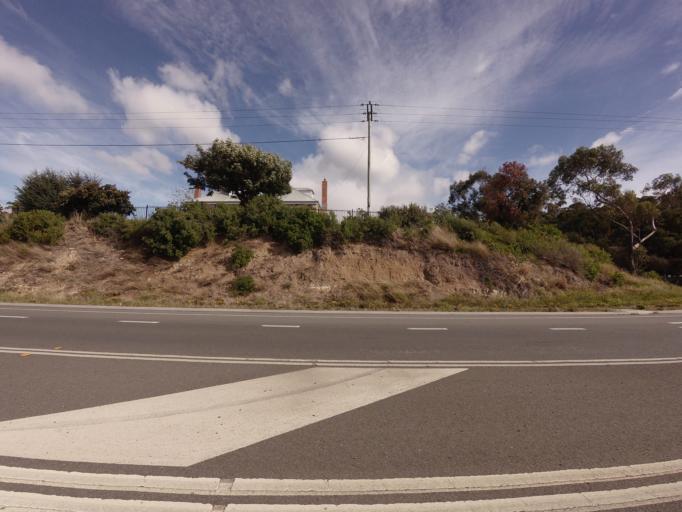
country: AU
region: Tasmania
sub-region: Glenorchy
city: Granton
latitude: -42.7489
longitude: 147.2223
